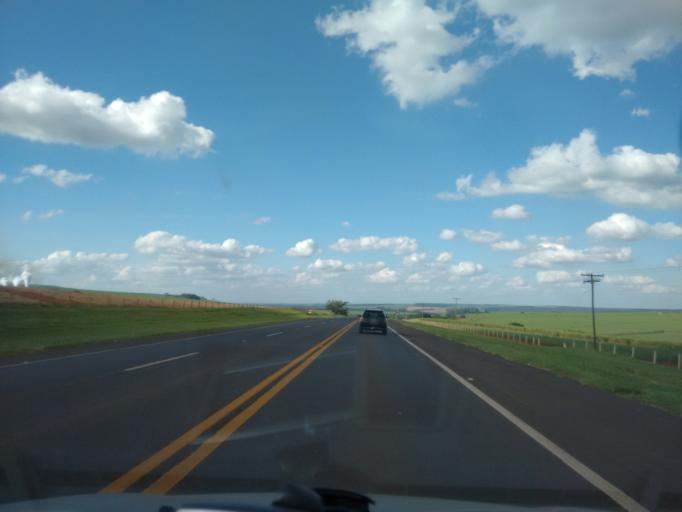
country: BR
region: Sao Paulo
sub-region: Americo Brasiliense
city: Americo Brasiliense
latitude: -21.7647
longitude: -48.0831
